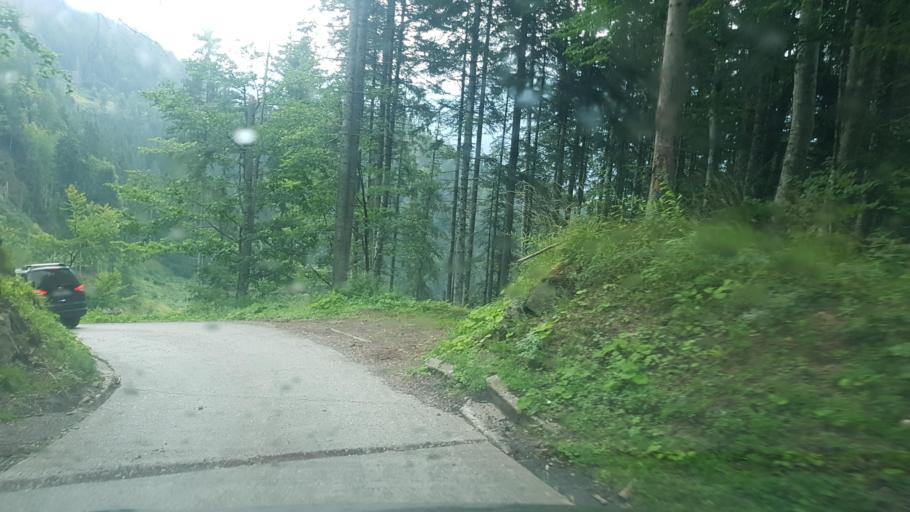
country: IT
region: Friuli Venezia Giulia
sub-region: Provincia di Udine
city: Rigolato
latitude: 46.5518
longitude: 12.8237
